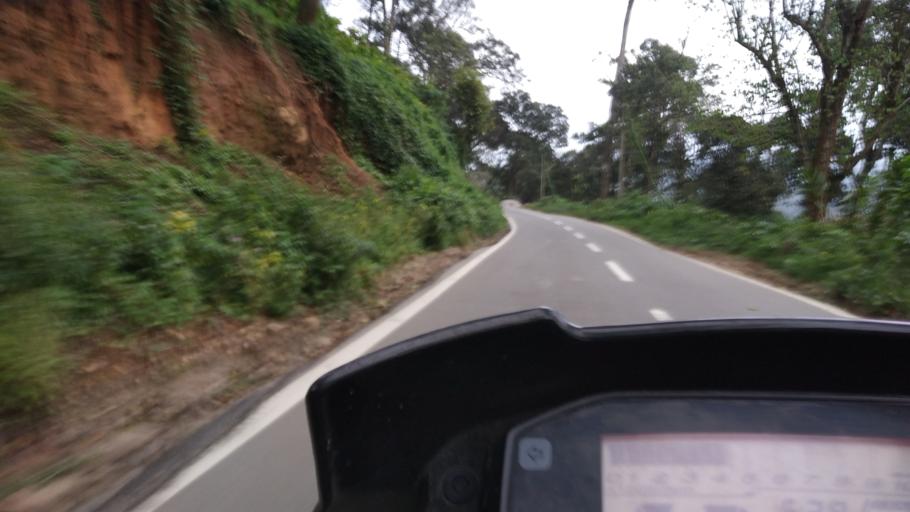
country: IN
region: Tamil Nadu
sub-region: Theni
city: Bodinayakkanur
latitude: 9.9976
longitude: 77.2188
